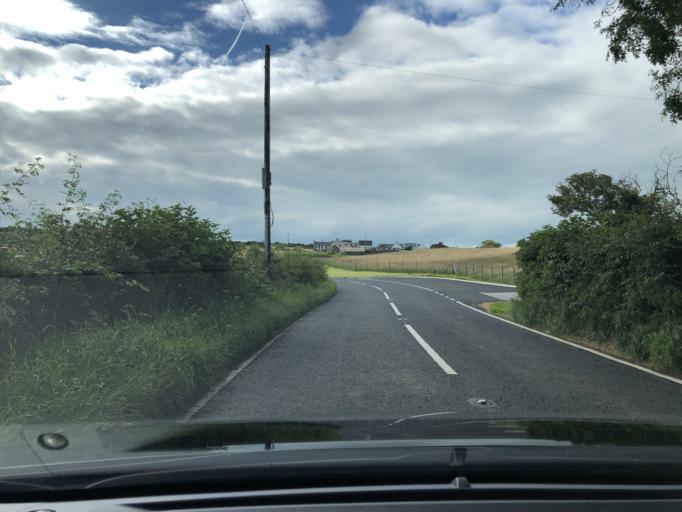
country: GB
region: Northern Ireland
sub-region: Down District
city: Dundrum
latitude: 54.2727
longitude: -5.7893
